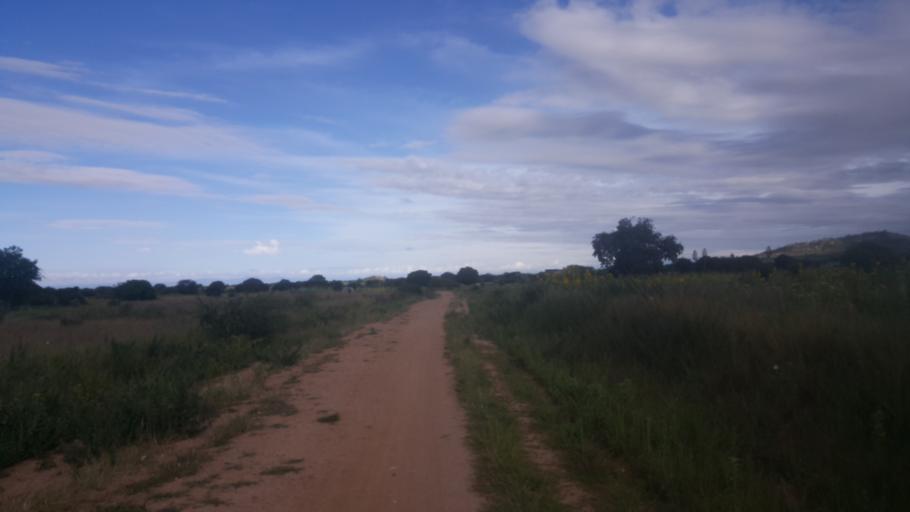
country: TZ
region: Dodoma
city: Dodoma
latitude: -6.0900
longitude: 35.5285
